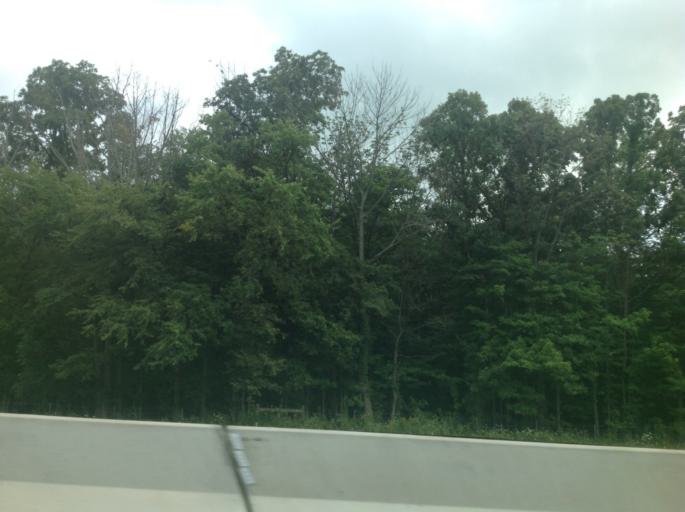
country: US
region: Ohio
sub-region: Morrow County
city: Mount Gilead
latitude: 40.4831
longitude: -82.7383
